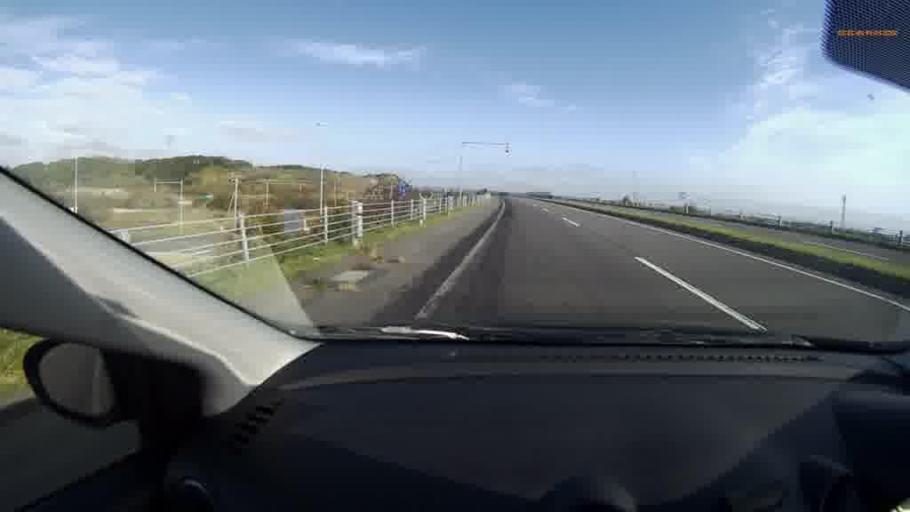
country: JP
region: Hokkaido
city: Kushiro
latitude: 43.0076
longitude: 144.2558
